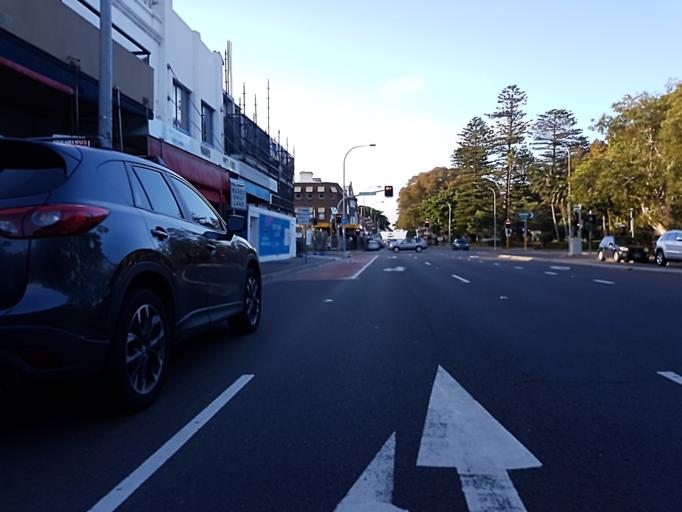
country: AU
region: New South Wales
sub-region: Manly Vale
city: Manly
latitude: -33.7963
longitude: 151.2852
